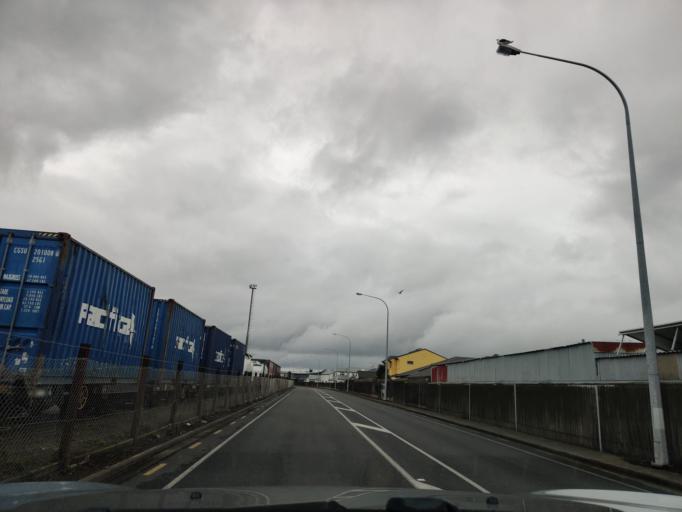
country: NZ
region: Hawke's Bay
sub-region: Napier City
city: Napier
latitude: -39.4799
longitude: 176.9038
